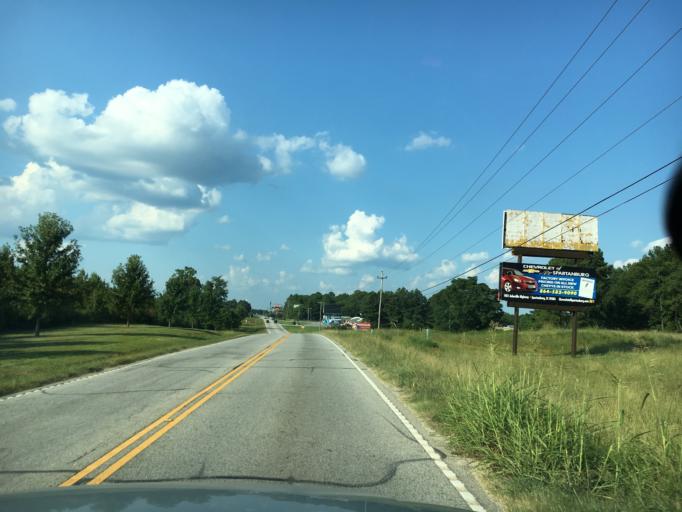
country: US
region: South Carolina
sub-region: Laurens County
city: Clinton
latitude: 34.4967
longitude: -81.8645
